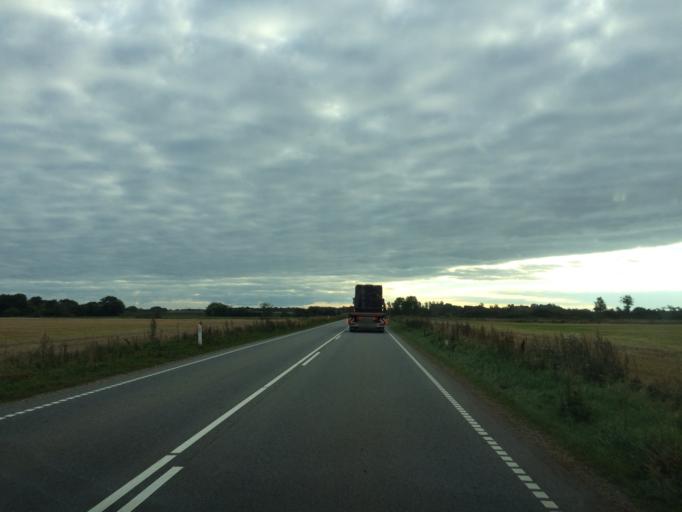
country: DK
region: Central Jutland
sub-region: Ringkobing-Skjern Kommune
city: Skjern
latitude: 55.9667
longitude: 8.5571
